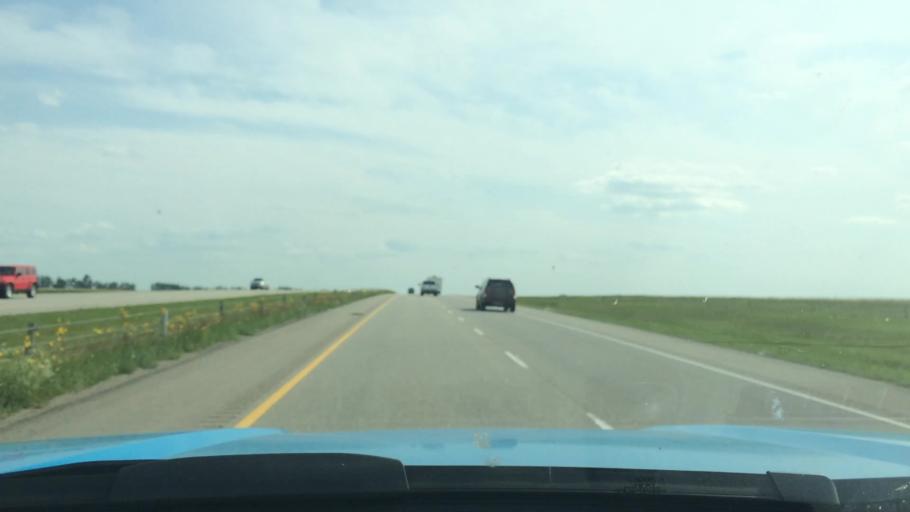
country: CA
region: Alberta
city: Carstairs
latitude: 51.6311
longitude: -114.0256
